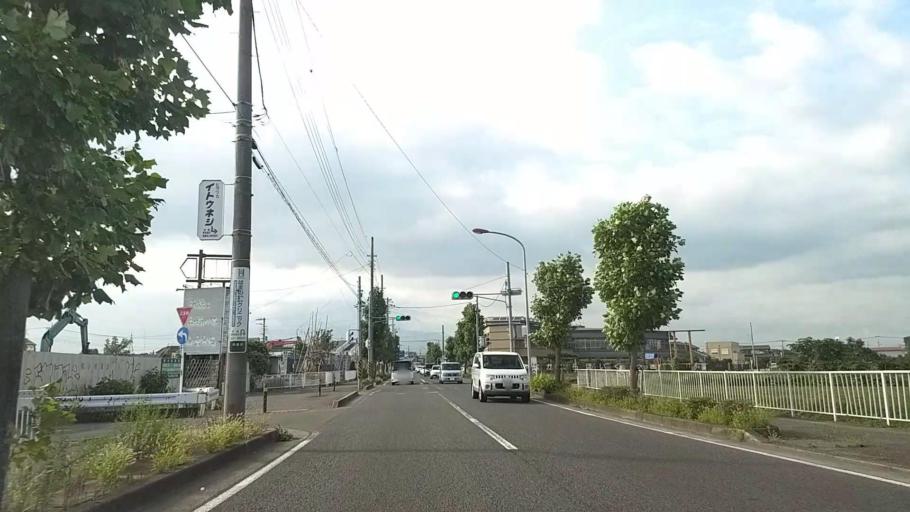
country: JP
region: Kanagawa
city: Hiratsuka
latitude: 35.3532
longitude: 139.3292
